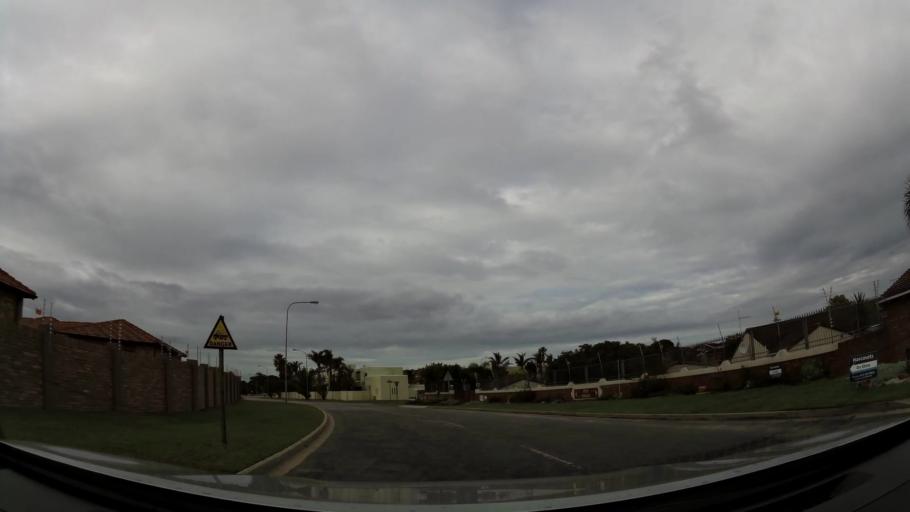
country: ZA
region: Eastern Cape
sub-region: Nelson Mandela Bay Metropolitan Municipality
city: Port Elizabeth
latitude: -33.9719
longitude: 25.6205
